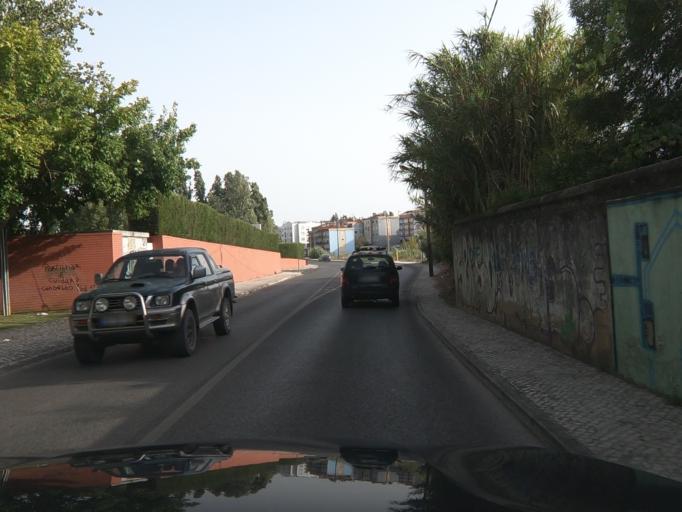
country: PT
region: Setubal
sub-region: Setubal
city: Setubal
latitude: 38.5381
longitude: -8.8983
